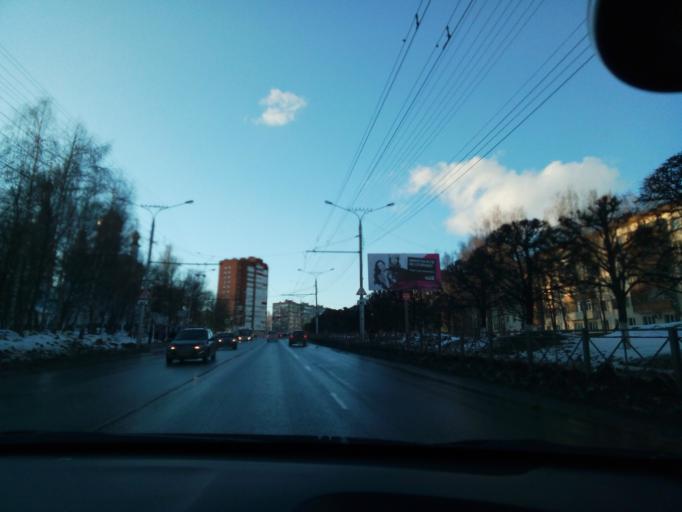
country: RU
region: Chuvashia
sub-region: Cheboksarskiy Rayon
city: Cheboksary
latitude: 56.1394
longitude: 47.1883
